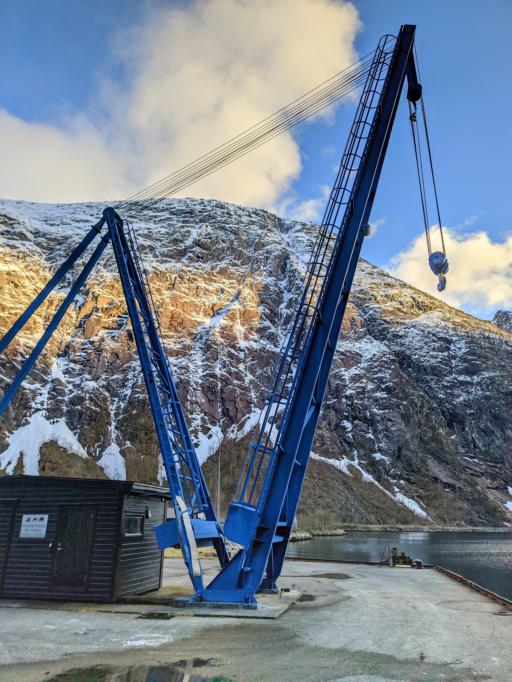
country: NO
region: Hordaland
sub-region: Eidfjord
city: Eidfjord
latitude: 60.4989
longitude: 7.1389
